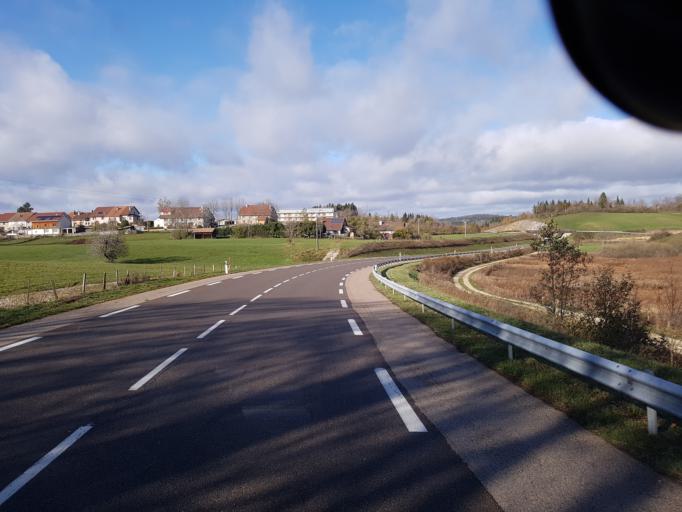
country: FR
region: Franche-Comte
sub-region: Departement du Jura
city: Morbier
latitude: 46.5791
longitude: 5.9618
